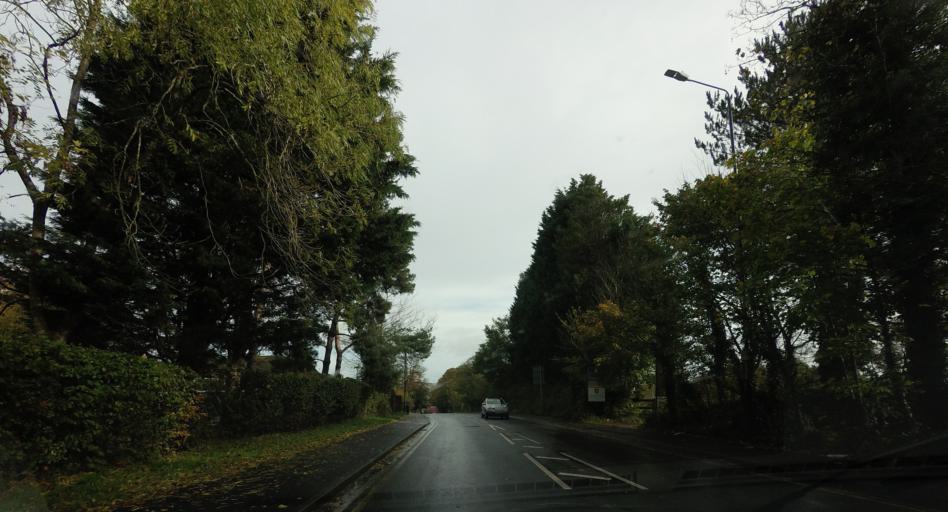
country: GB
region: England
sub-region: Kent
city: Sevenoaks
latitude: 51.2811
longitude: 0.1649
